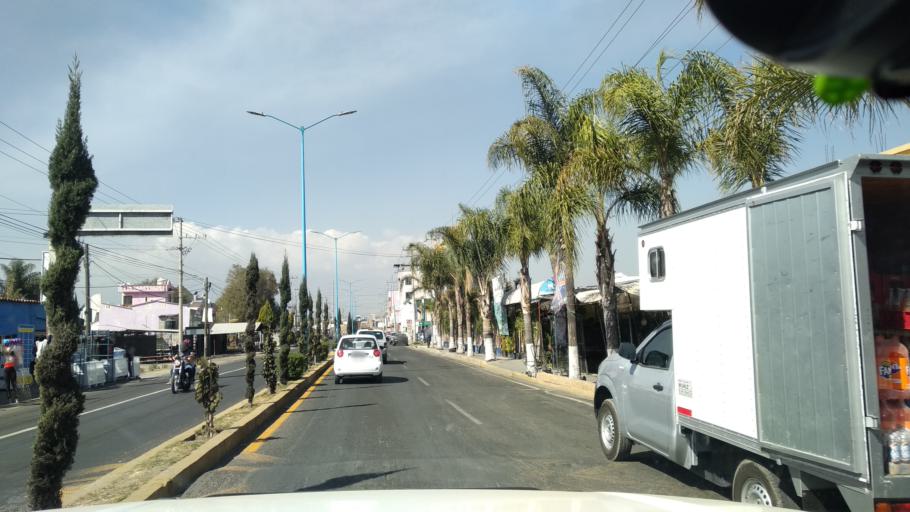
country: MX
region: Puebla
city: San Martin Texmelucan de Labastida
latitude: 19.2933
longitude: -98.4065
